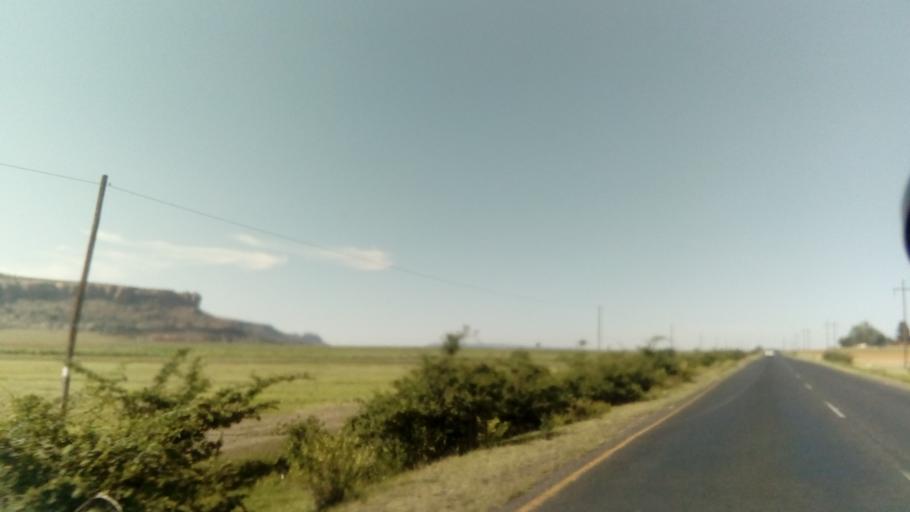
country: LS
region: Berea
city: Teyateyaneng
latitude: -29.1657
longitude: 27.6454
